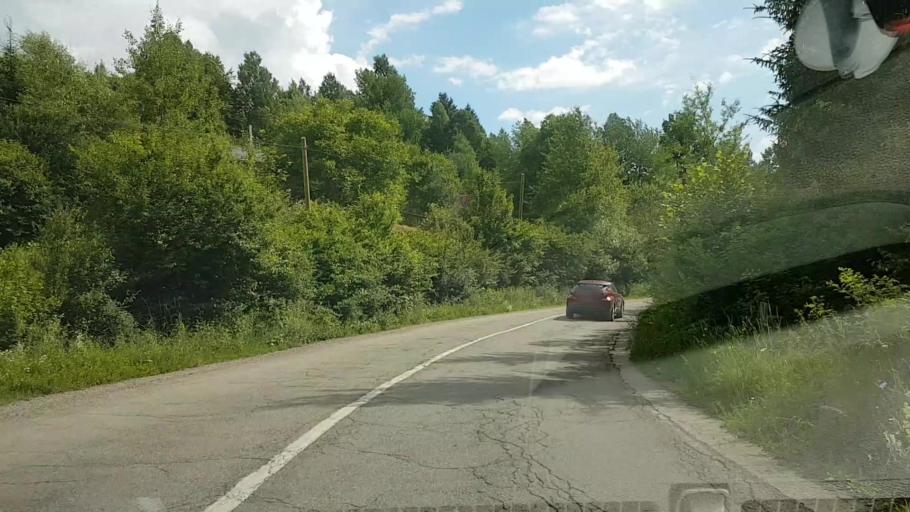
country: RO
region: Neamt
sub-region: Comuna Hangu
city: Hangu
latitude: 47.0502
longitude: 26.0413
